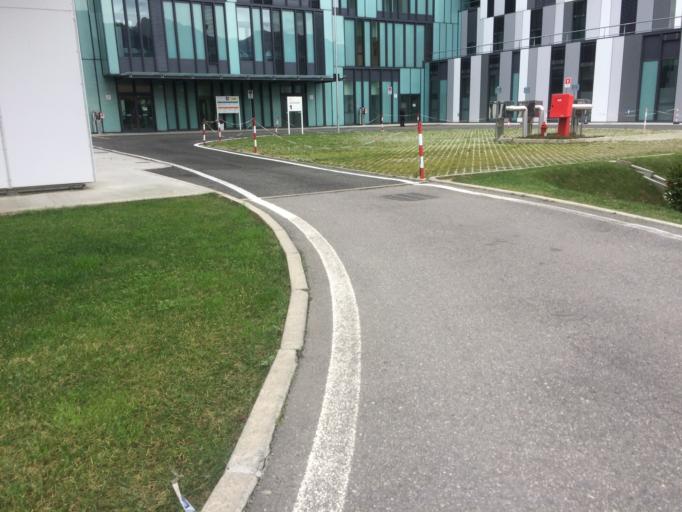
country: IT
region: Tuscany
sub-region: Provincia di Massa-Carrara
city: Massa
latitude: 44.0199
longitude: 10.1007
